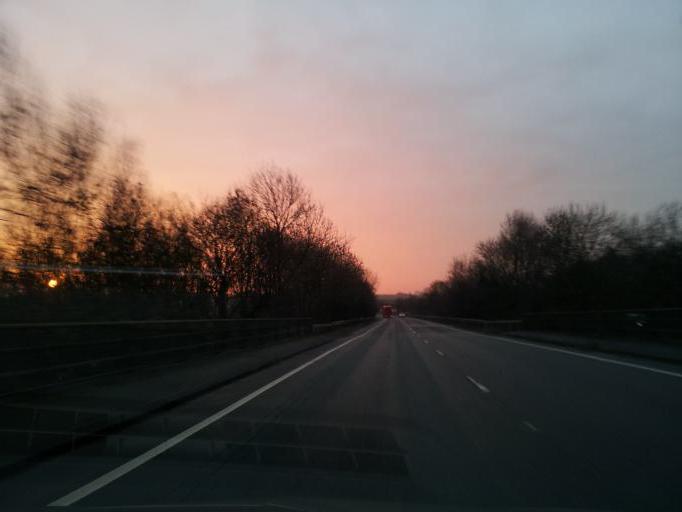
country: GB
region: England
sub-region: Peterborough
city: Wansford
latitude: 52.5816
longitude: -0.4126
